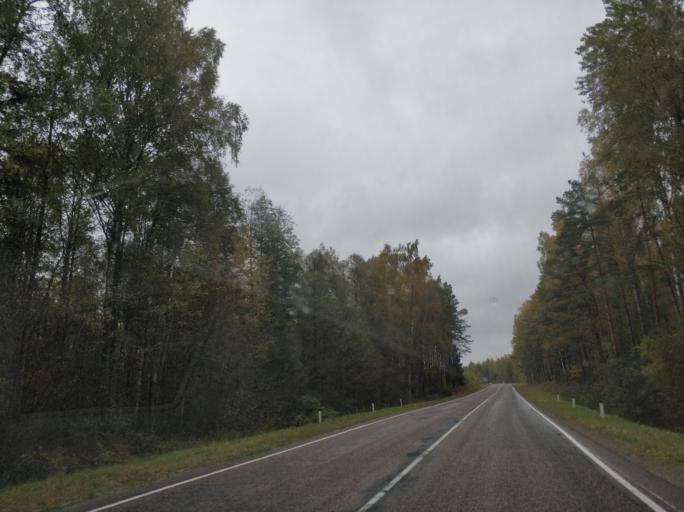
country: RU
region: Pskov
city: Opochka
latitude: 56.5060
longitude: 28.6623
